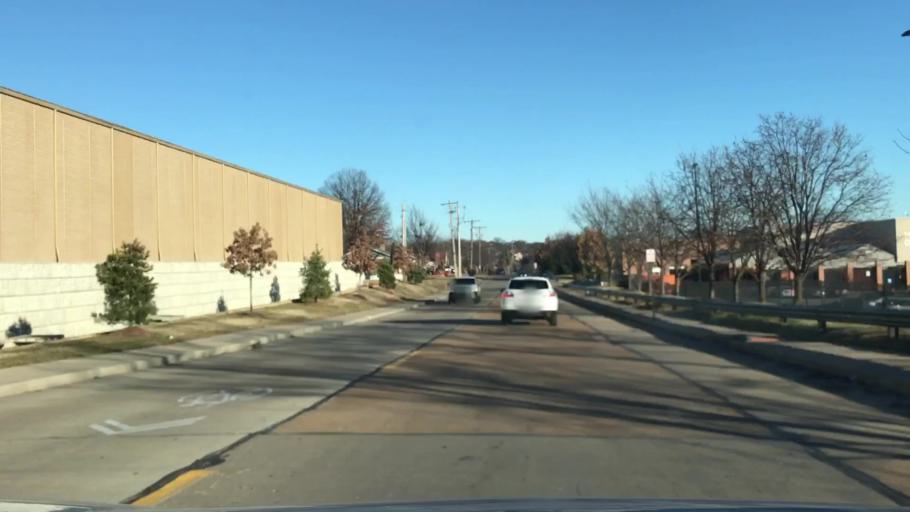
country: US
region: Missouri
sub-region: Saint Louis County
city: Maplewood
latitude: 38.6227
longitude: -90.3329
